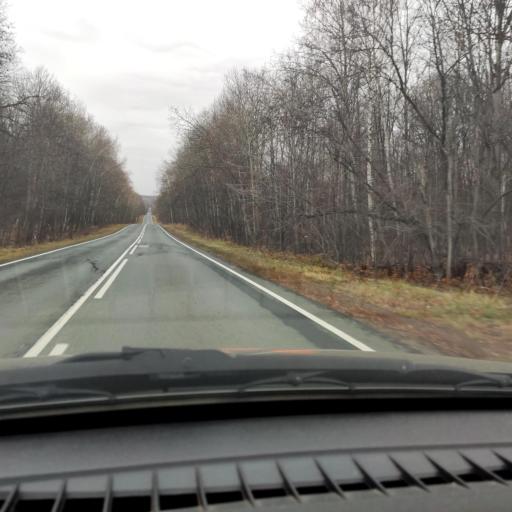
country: RU
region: Samara
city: Zhigulevsk
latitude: 53.3432
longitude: 49.5416
